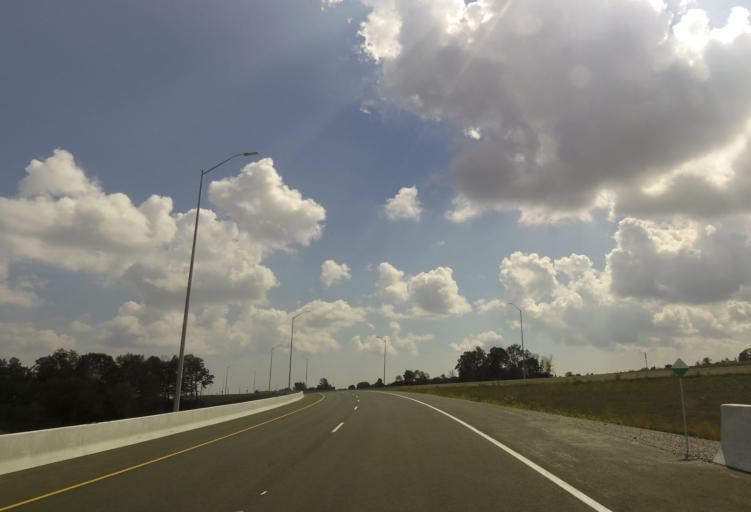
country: CA
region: Ontario
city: Ajax
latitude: 43.9488
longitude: -79.0105
